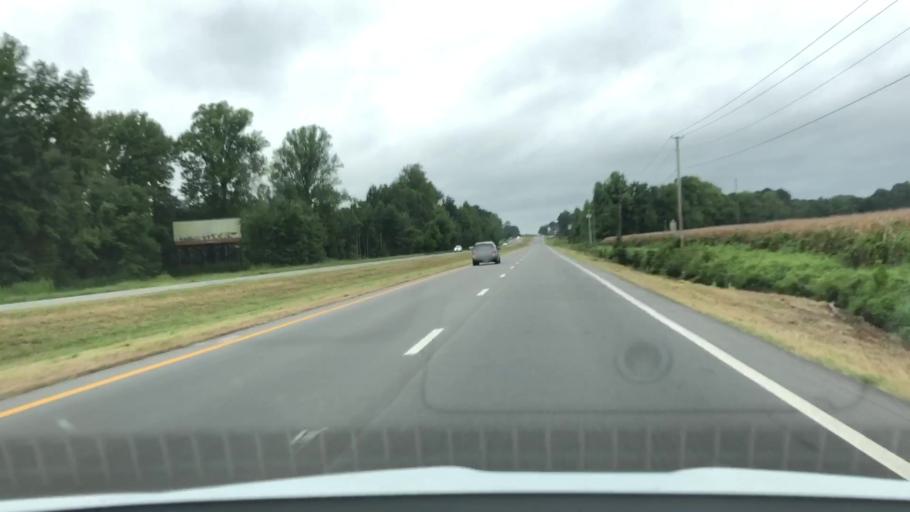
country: US
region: North Carolina
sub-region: Lenoir County
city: La Grange
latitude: 35.2714
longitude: -77.7412
